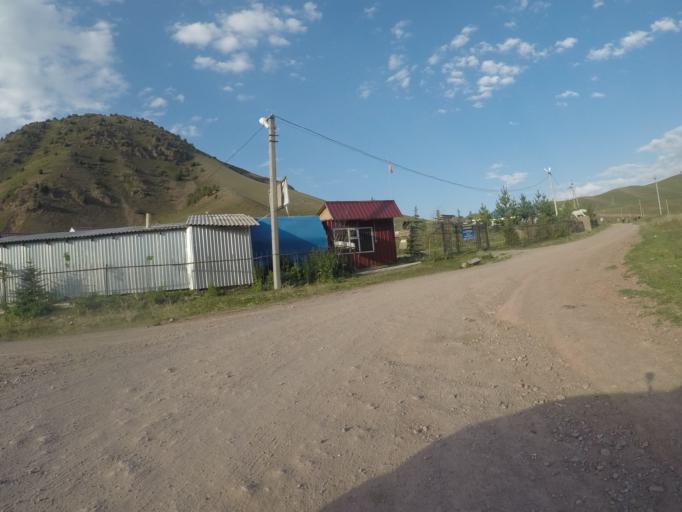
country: KG
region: Chuy
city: Bishkek
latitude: 42.6412
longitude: 74.6204
